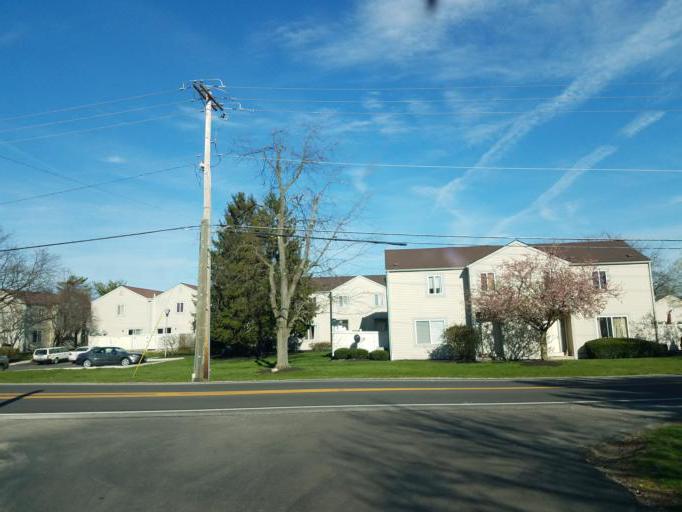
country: US
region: Ohio
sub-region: Franklin County
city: Dublin
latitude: 40.0631
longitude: -83.0753
